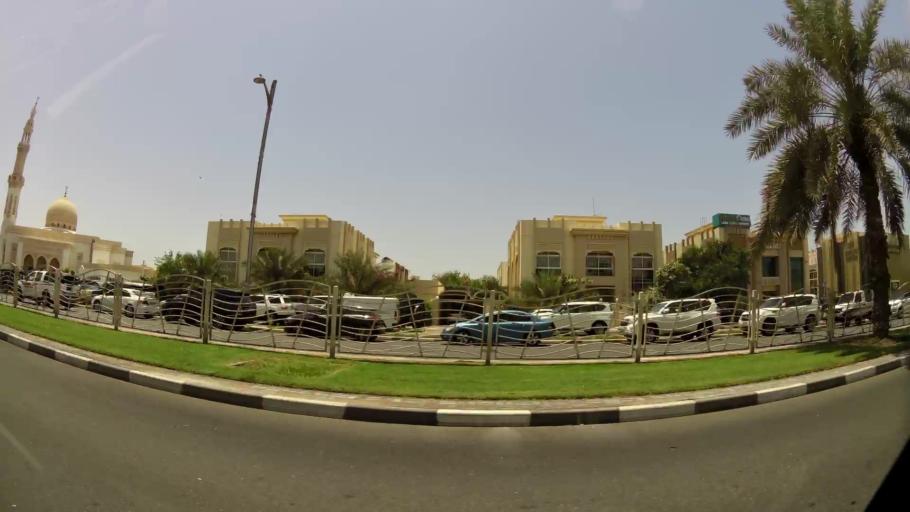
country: AE
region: Dubai
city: Dubai
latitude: 25.2083
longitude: 55.2455
